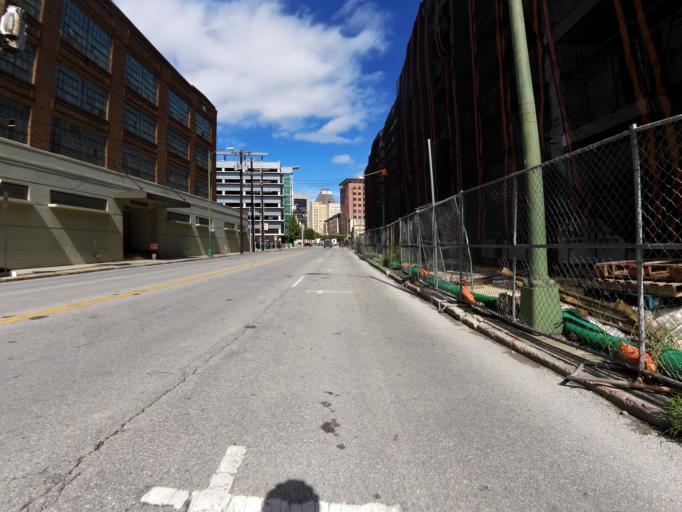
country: US
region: Texas
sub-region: Bexar County
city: San Antonio
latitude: 29.4209
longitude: -98.4959
